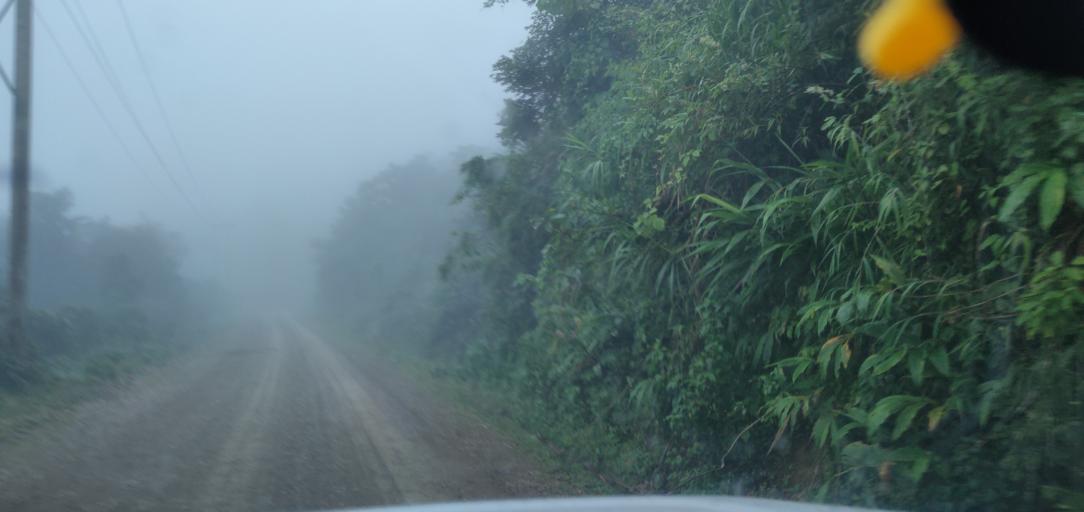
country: LA
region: Phongsali
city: Phongsali
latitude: 21.3892
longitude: 102.1981
